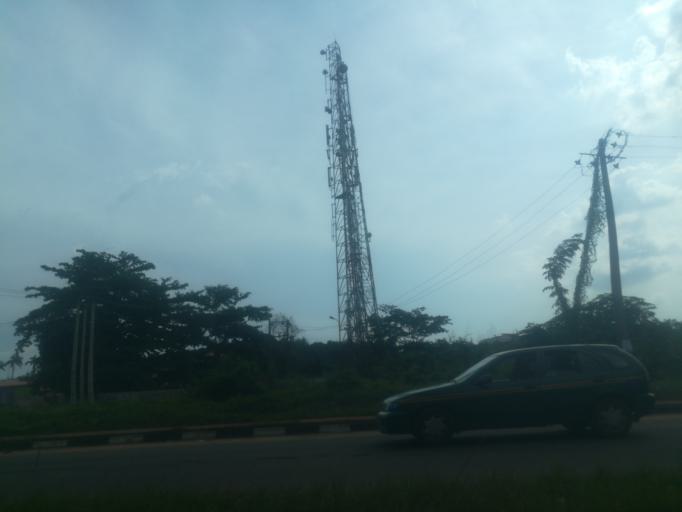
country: NG
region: Ogun
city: Abeokuta
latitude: 7.1354
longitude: 3.3473
